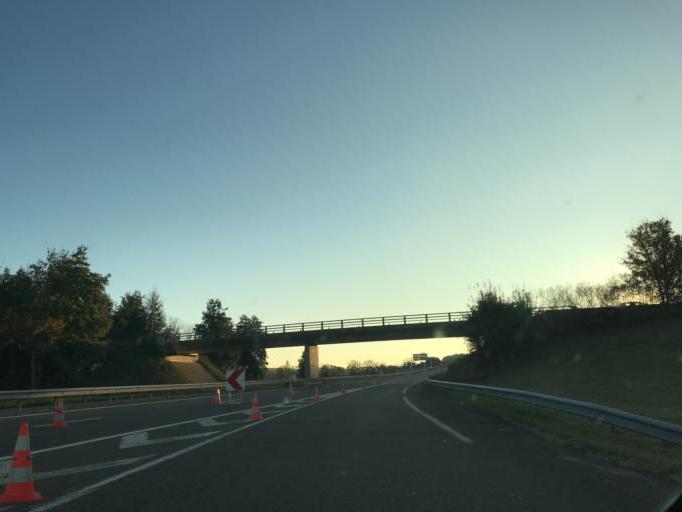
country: FR
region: Bourgogne
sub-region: Departement de l'Yonne
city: Saint-Martin-du-Tertre
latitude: 48.2412
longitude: 3.2605
